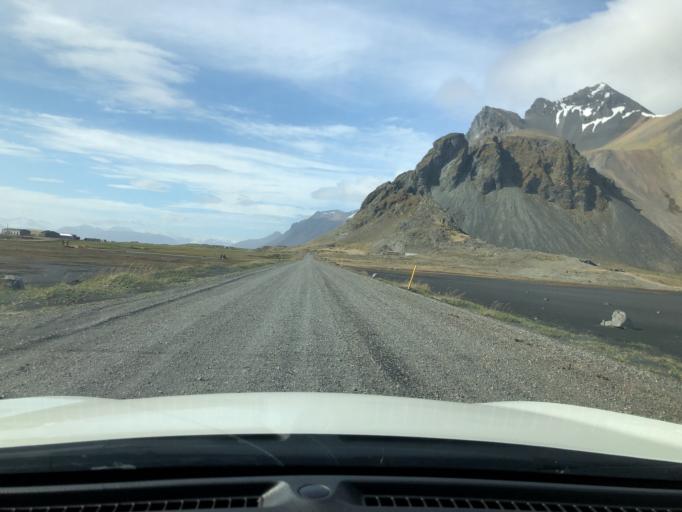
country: IS
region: East
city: Hoefn
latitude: 64.2511
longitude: -14.9870
